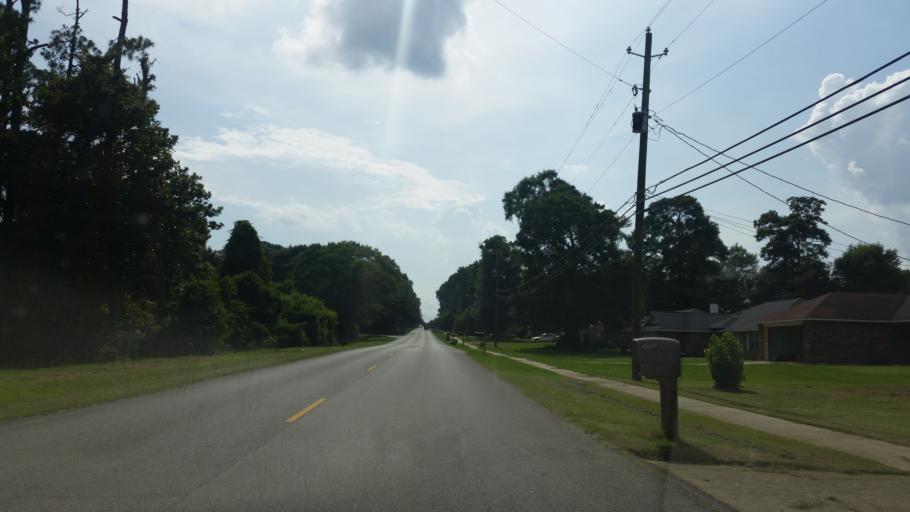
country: US
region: Florida
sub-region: Escambia County
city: Gonzalez
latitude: 30.5692
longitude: -87.2546
